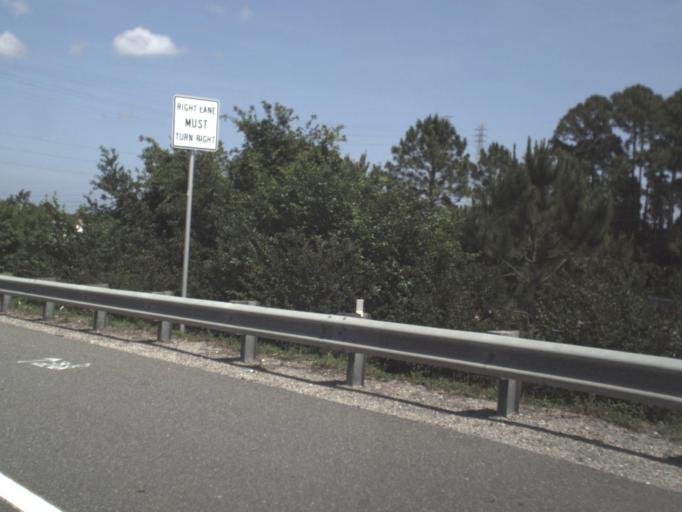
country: US
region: Florida
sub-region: Duval County
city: Jacksonville
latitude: 30.4127
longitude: -81.5467
